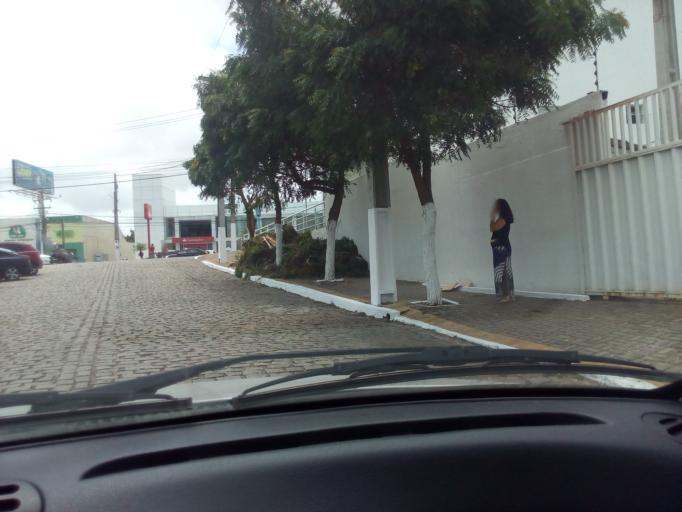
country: BR
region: Rio Grande do Norte
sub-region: Natal
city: Natal
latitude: -5.8538
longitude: -35.2005
